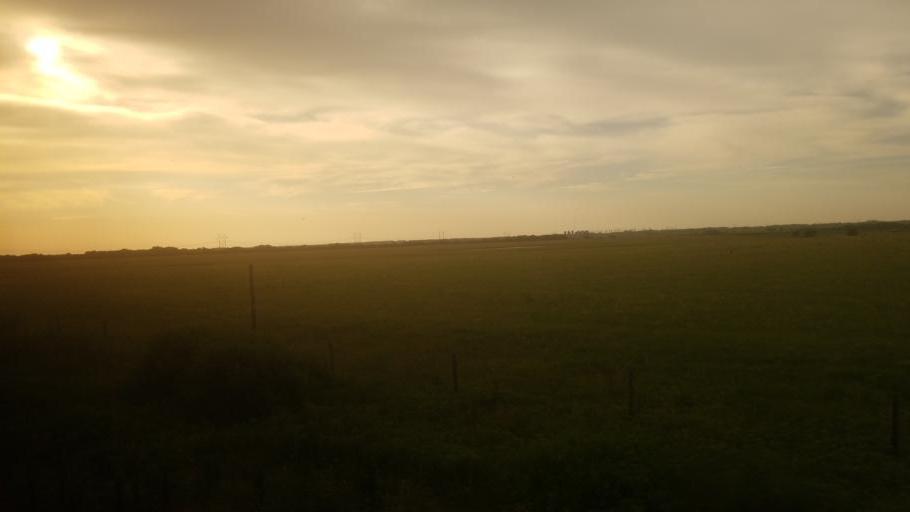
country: US
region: Kansas
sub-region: Lyon County
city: Emporia
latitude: 38.4538
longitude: -96.0921
